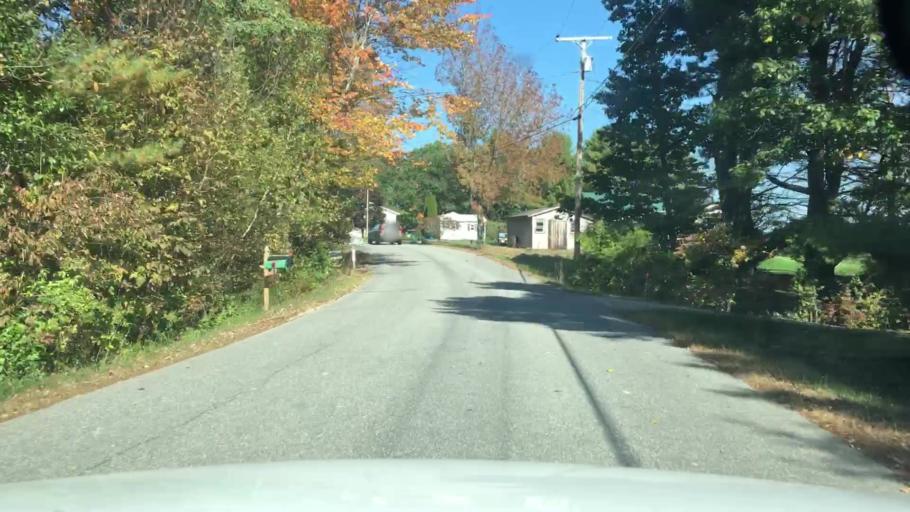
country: US
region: Maine
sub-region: Androscoggin County
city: Lisbon Falls
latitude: 44.0313
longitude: -69.9865
